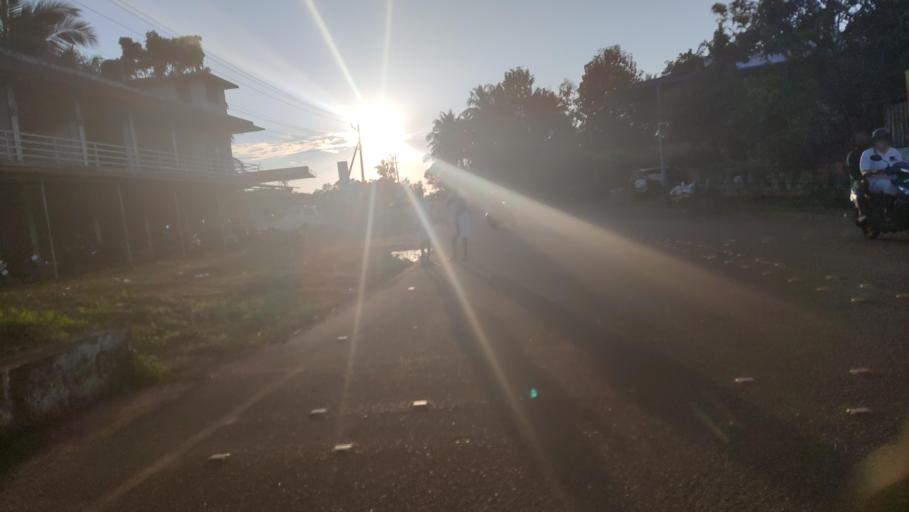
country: IN
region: Kerala
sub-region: Kasaragod District
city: Kannangad
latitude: 12.4040
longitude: 75.0964
